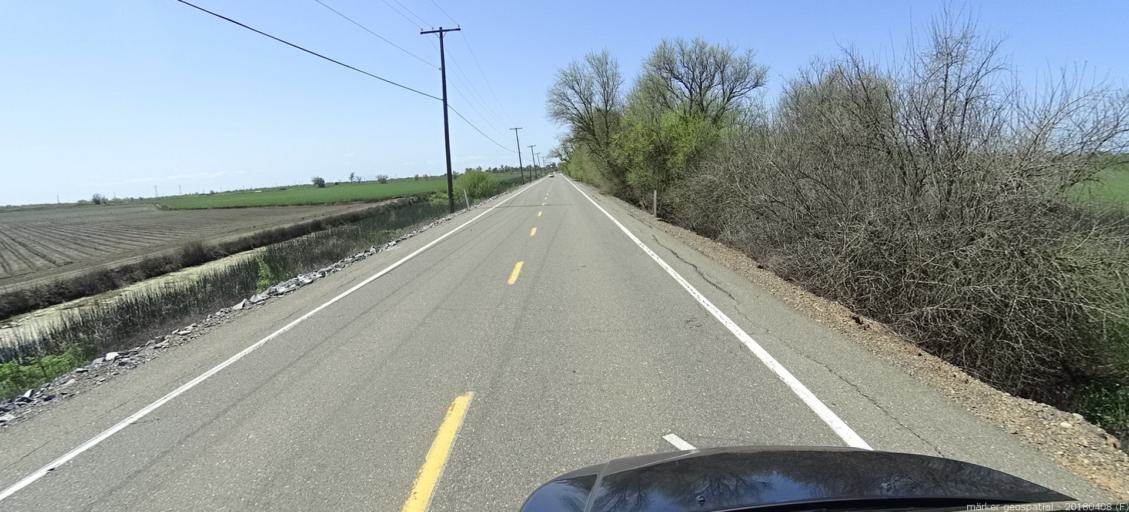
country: US
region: California
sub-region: Sacramento County
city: Laguna
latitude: 38.3689
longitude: -121.5024
